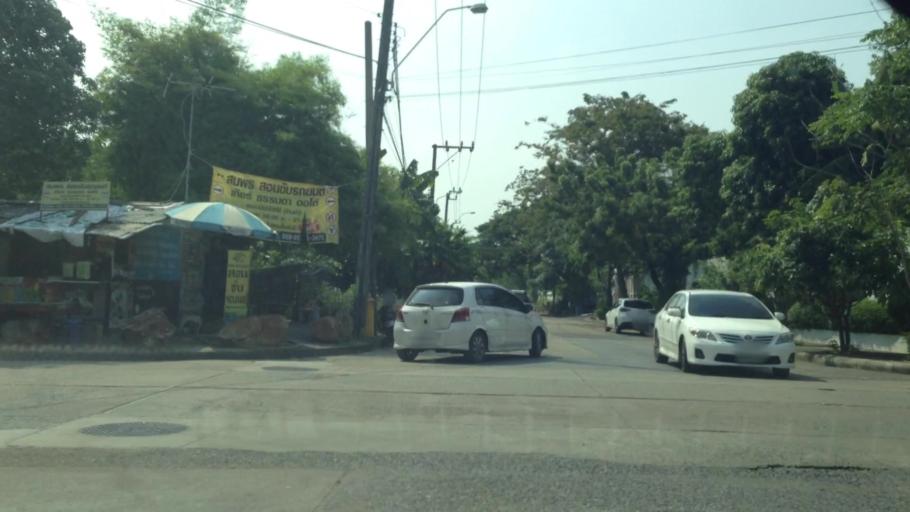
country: TH
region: Bangkok
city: Bang Na
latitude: 13.6858
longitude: 100.6576
